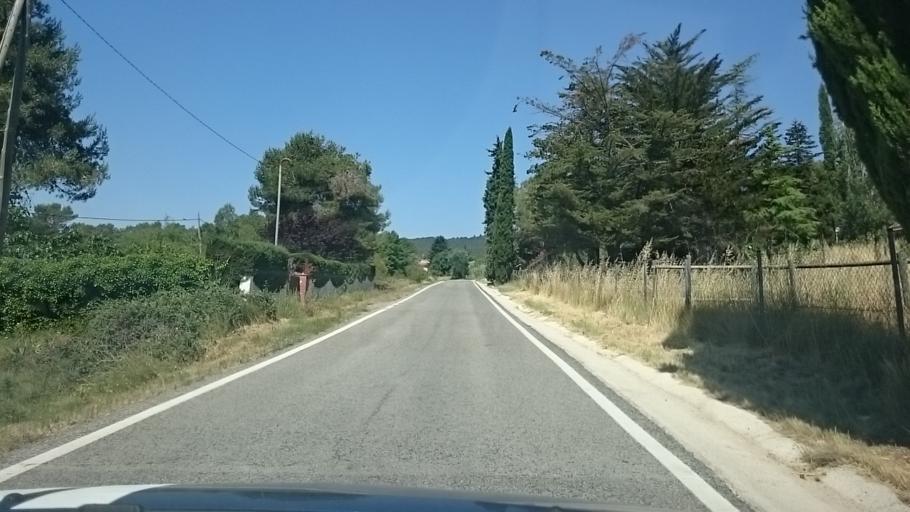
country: ES
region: Catalonia
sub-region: Provincia de Tarragona
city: Querol
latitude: 41.3972
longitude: 1.4506
